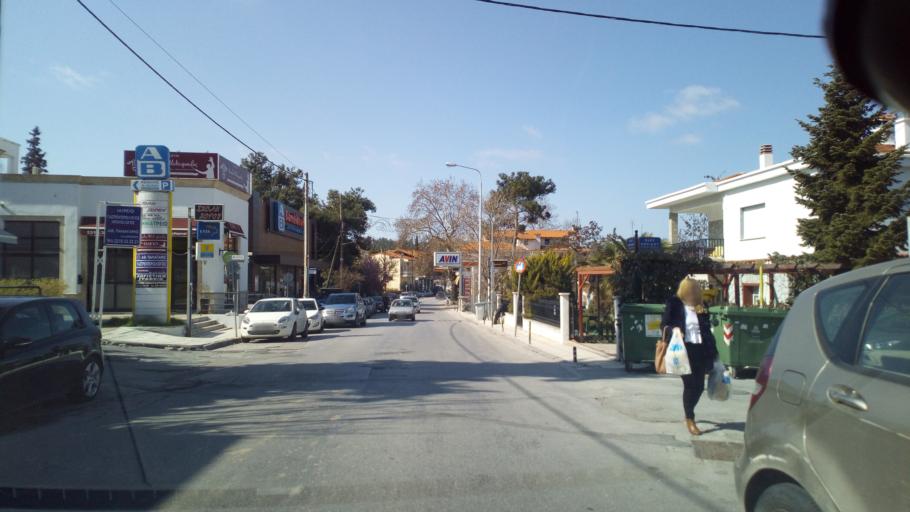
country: GR
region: Central Macedonia
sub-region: Nomos Thessalonikis
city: Panorama
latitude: 40.5918
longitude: 23.0400
